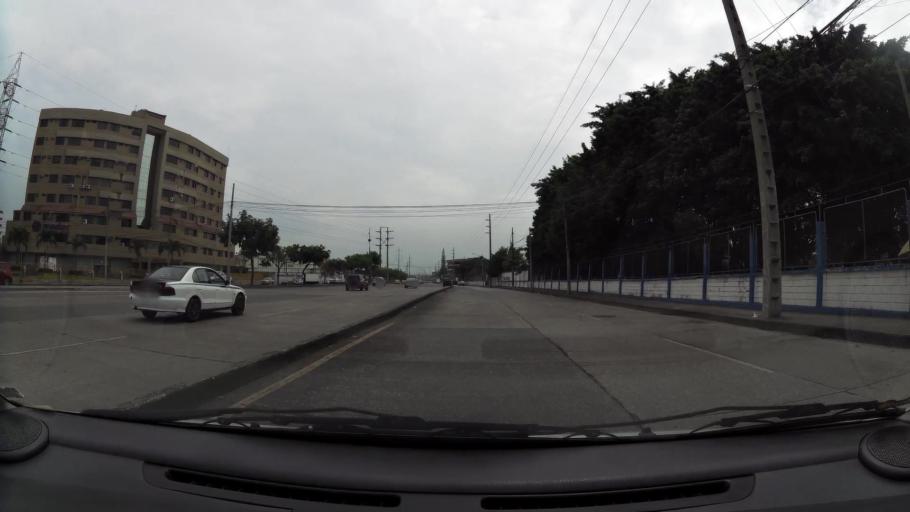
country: EC
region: Guayas
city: Eloy Alfaro
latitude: -2.1515
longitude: -79.8966
